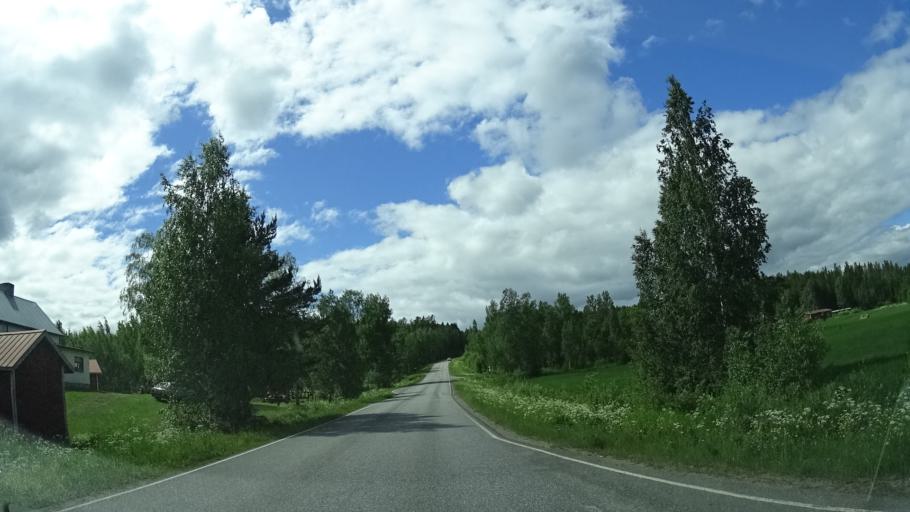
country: FI
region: Central Finland
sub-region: Joutsa
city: Luhanka
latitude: 61.8373
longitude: 25.7423
